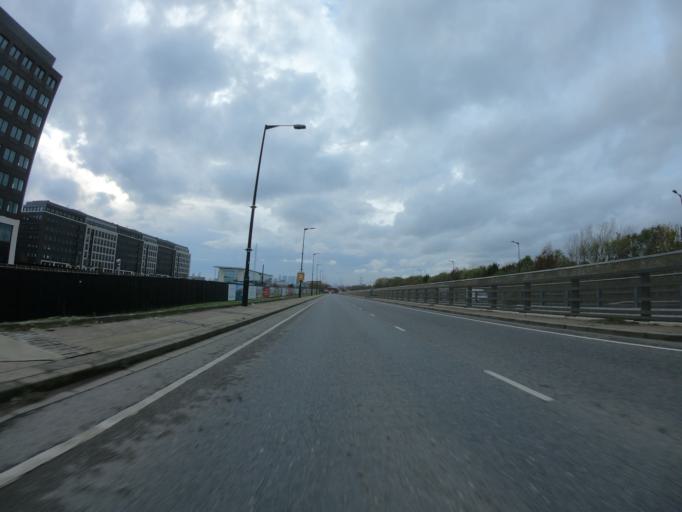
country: GB
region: England
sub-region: Greater London
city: Woolwich
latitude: 51.5088
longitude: 0.0531
